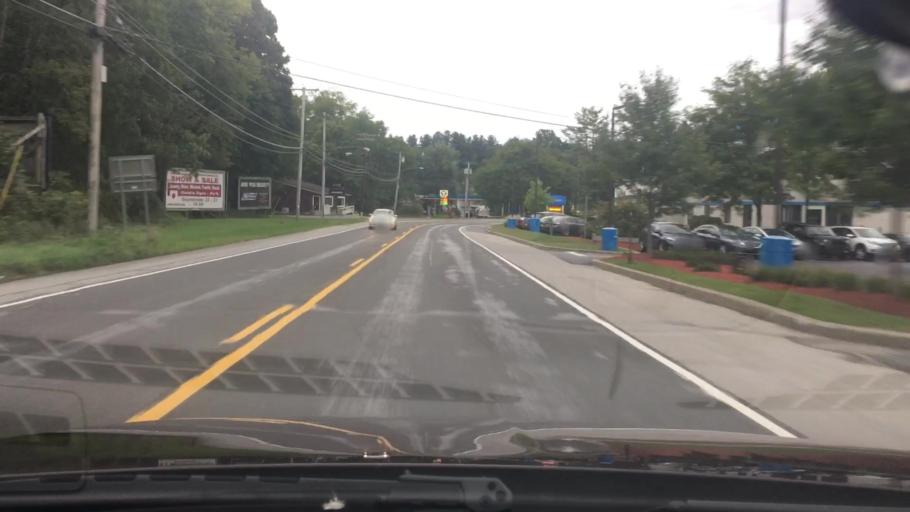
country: US
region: New York
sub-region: Dutchess County
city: Pleasant Valley
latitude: 41.7190
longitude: -73.8514
